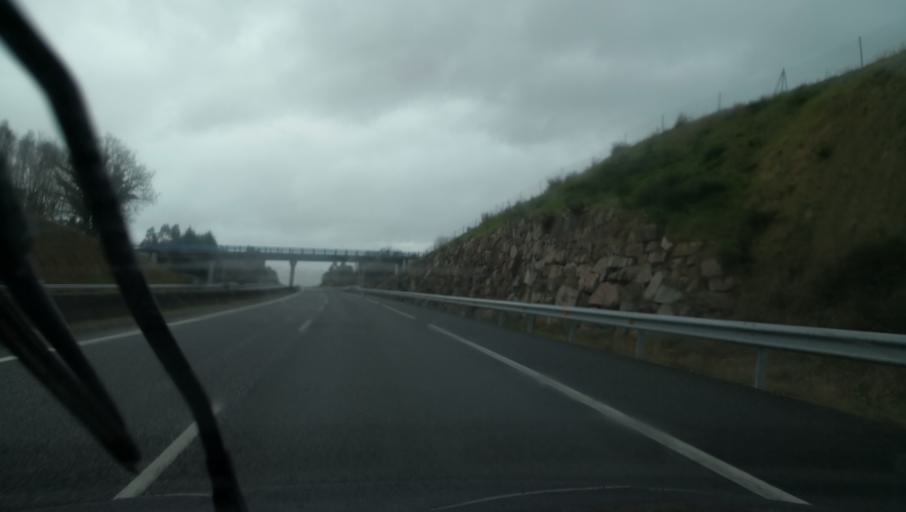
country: ES
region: Galicia
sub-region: Provincia de Pontevedra
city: Silleda
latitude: 42.6901
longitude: -8.1799
